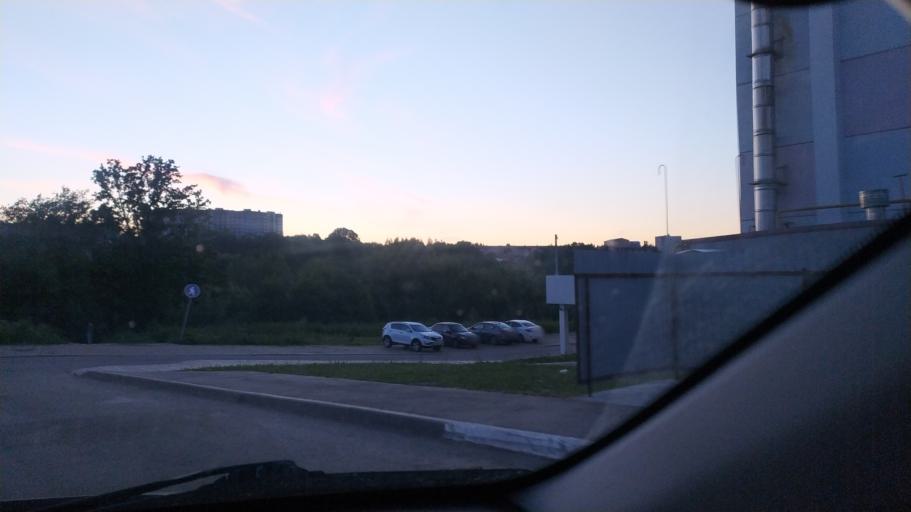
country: RU
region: Chuvashia
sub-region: Cheboksarskiy Rayon
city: Cheboksary
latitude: 56.1173
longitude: 47.2069
